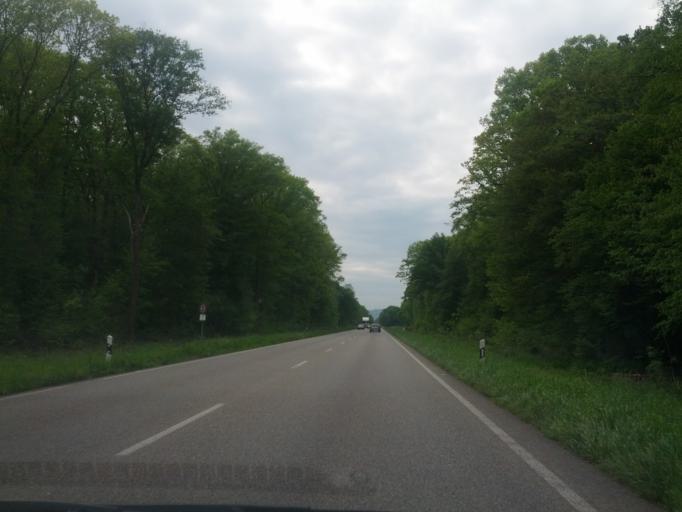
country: DE
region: Baden-Wuerttemberg
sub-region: Freiburg Region
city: Vorstetten
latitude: 48.0522
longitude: 7.8459
